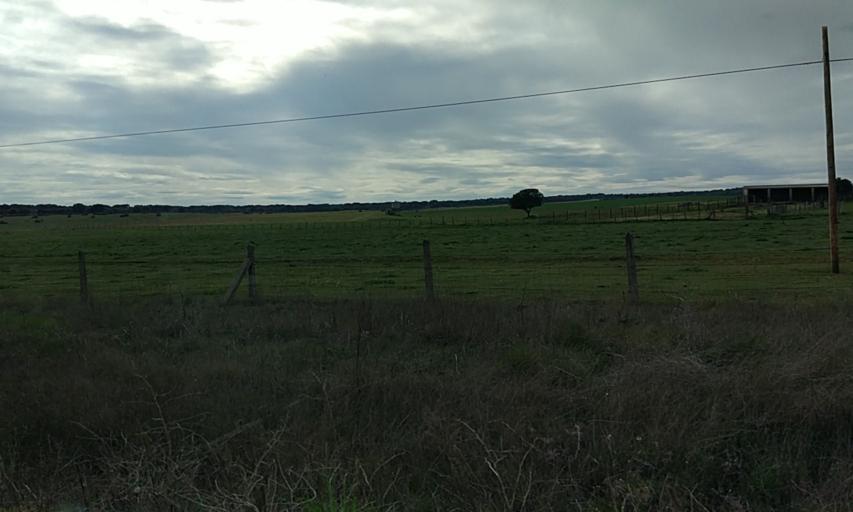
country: ES
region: Castille and Leon
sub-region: Provincia de Salamanca
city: Herguijuela de Ciudad Rodrigo
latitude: 40.4704
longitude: -6.5825
